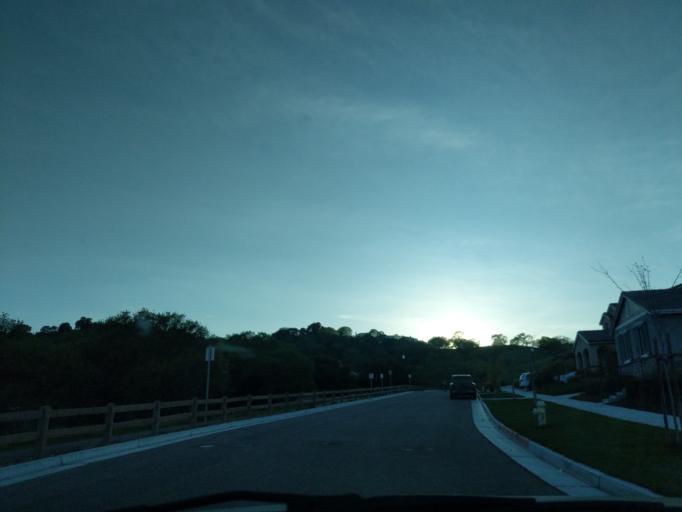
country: US
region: California
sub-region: Santa Clara County
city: Gilroy
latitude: 37.0282
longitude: -121.6127
